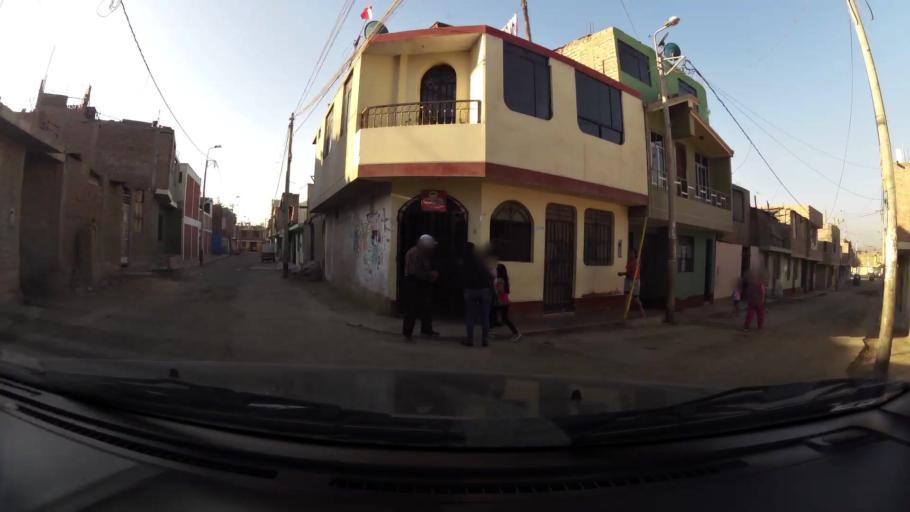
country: PE
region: Ica
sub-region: Provincia de Ica
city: Ica
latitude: -14.0573
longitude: -75.7292
